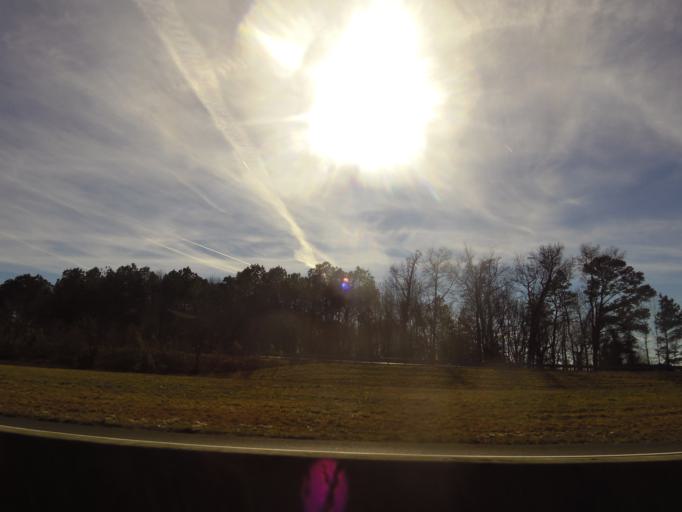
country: US
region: Virginia
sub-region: Isle of Wight County
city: Smithfield
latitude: 36.9714
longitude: -76.6341
